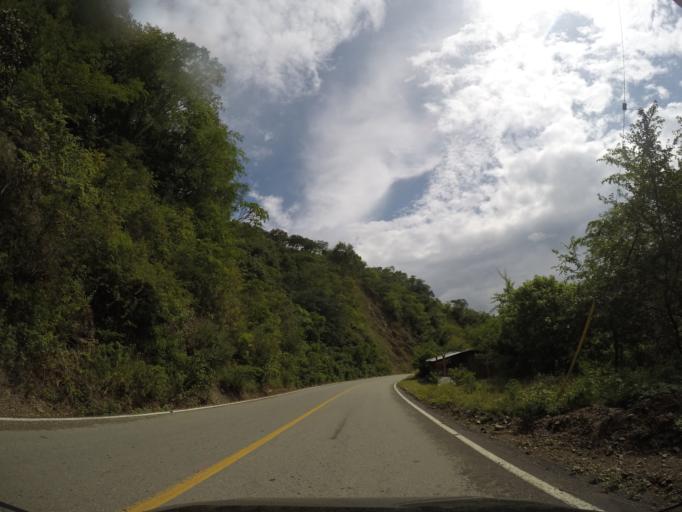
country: MX
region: Oaxaca
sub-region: San Jeronimo Coatlan
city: San Cristobal Honduras
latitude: 16.3784
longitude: -97.0767
